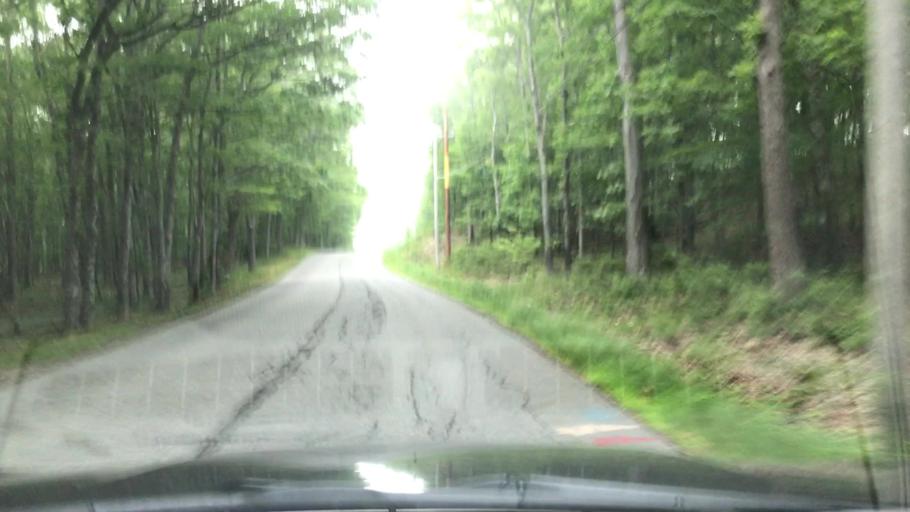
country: US
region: Maine
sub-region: Hancock County
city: Bar Harbor
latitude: 44.3483
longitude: -68.1817
